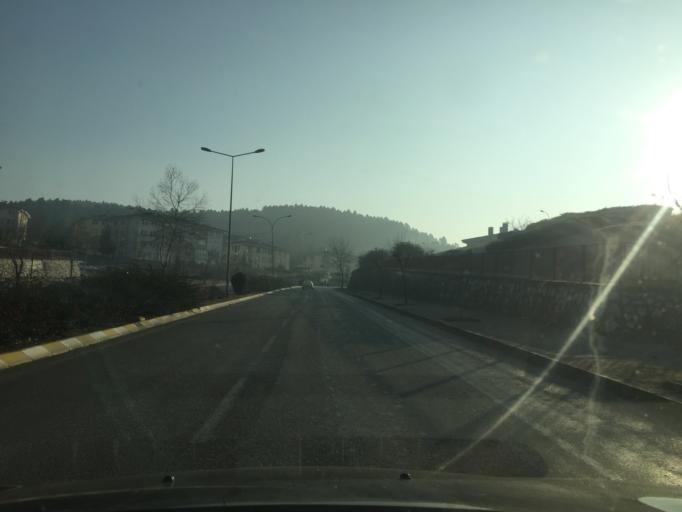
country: TR
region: Duzce
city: Duzce
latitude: 40.8681
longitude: 31.2285
